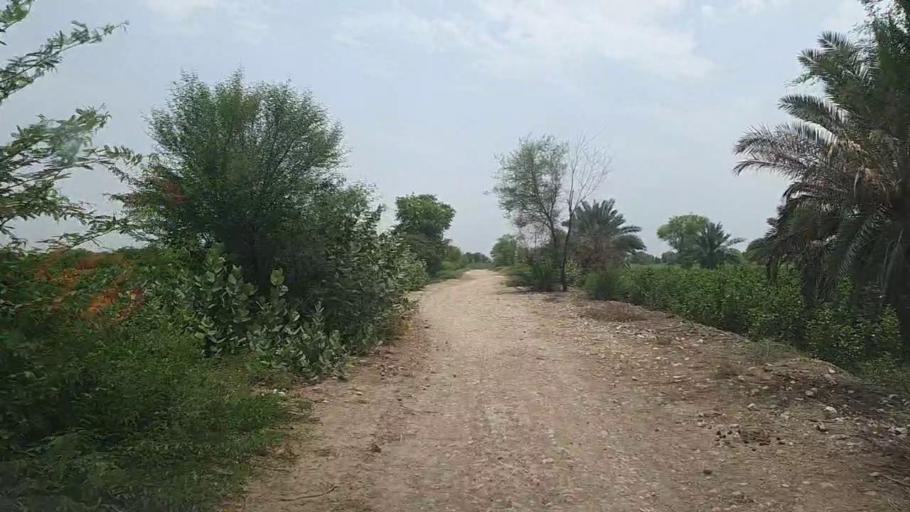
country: PK
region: Sindh
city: Karaundi
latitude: 26.9134
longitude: 68.3230
